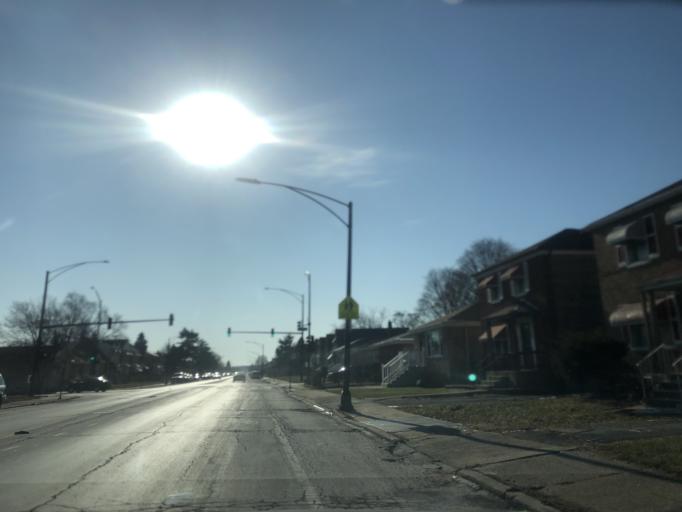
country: US
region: Illinois
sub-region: Cook County
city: Evergreen Park
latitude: 41.7564
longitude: -87.6733
